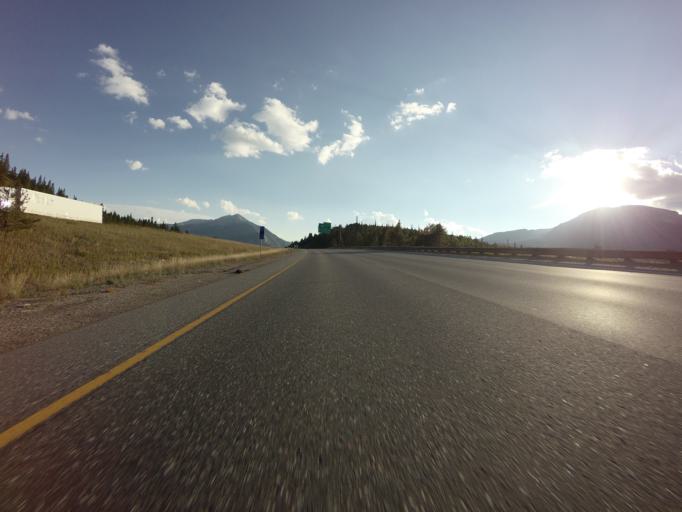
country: US
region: Colorado
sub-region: Summit County
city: Silverthorne
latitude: 39.6093
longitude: -106.0800
